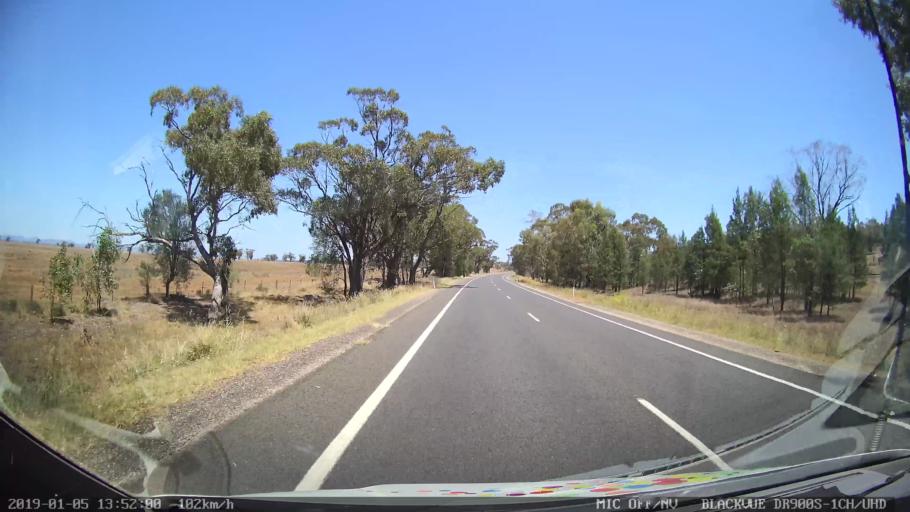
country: AU
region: New South Wales
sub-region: Gunnedah
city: Gunnedah
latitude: -31.0531
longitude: 150.2778
